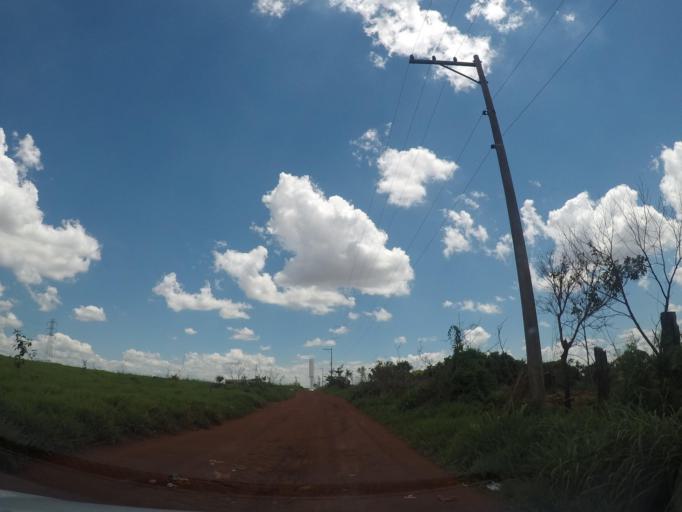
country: BR
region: Sao Paulo
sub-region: Hortolandia
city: Hortolandia
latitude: -22.8430
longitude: -47.2419
